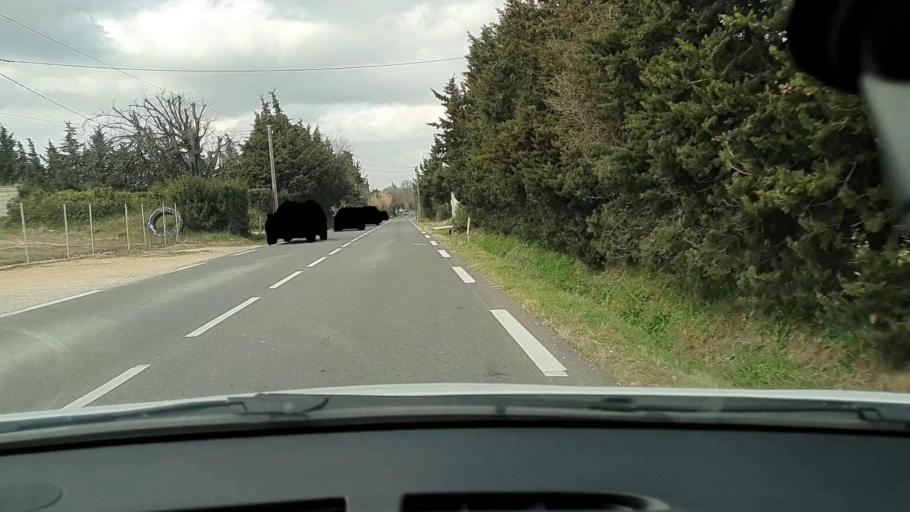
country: FR
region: Languedoc-Roussillon
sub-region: Departement du Gard
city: Sernhac
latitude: 43.9002
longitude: 4.5712
